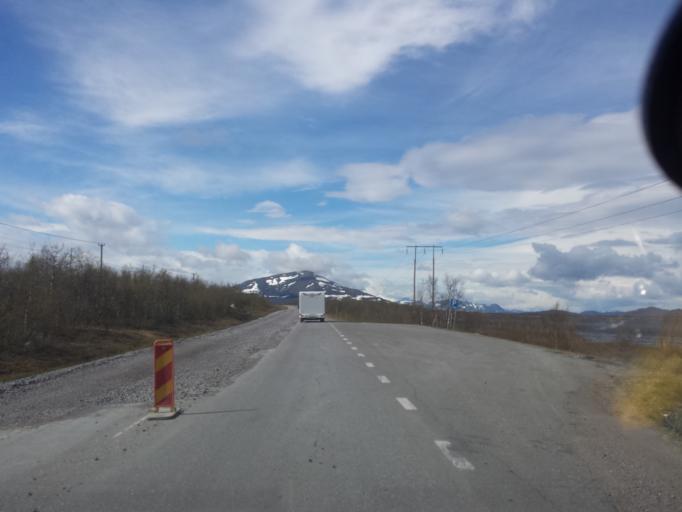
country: SE
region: Norrbotten
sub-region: Kiruna Kommun
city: Kiruna
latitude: 68.1118
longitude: 19.8334
